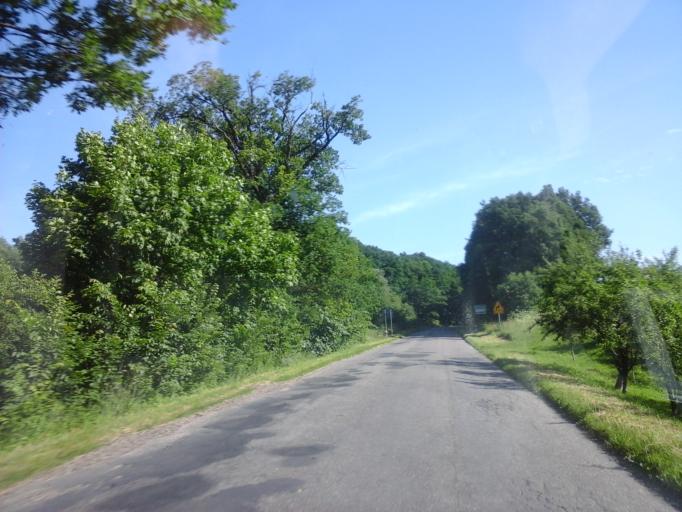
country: PL
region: West Pomeranian Voivodeship
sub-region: Powiat swidwinski
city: Polczyn-Zdroj
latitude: 53.6760
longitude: 16.0181
